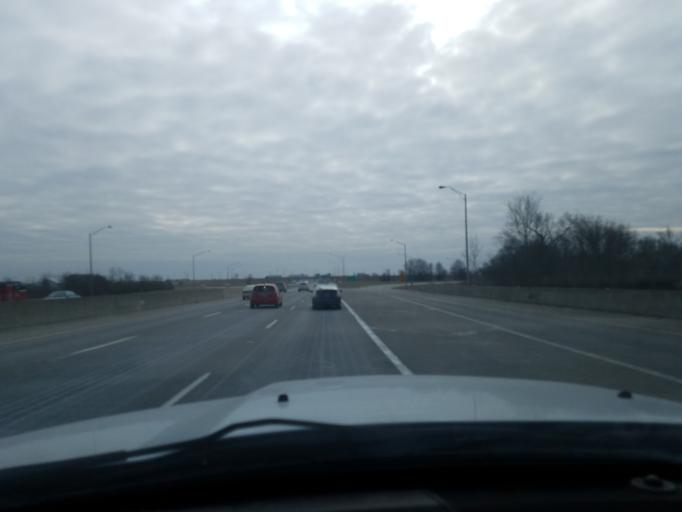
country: US
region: Indiana
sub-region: Clark County
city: Sellersburg
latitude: 38.3517
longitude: -85.7546
